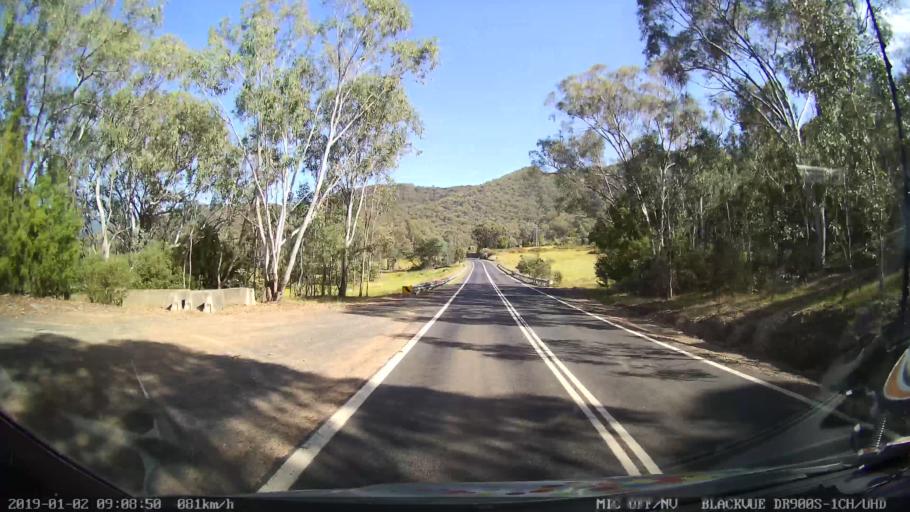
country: AU
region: New South Wales
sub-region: Tumut Shire
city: Tumut
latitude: -35.5288
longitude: 148.2869
